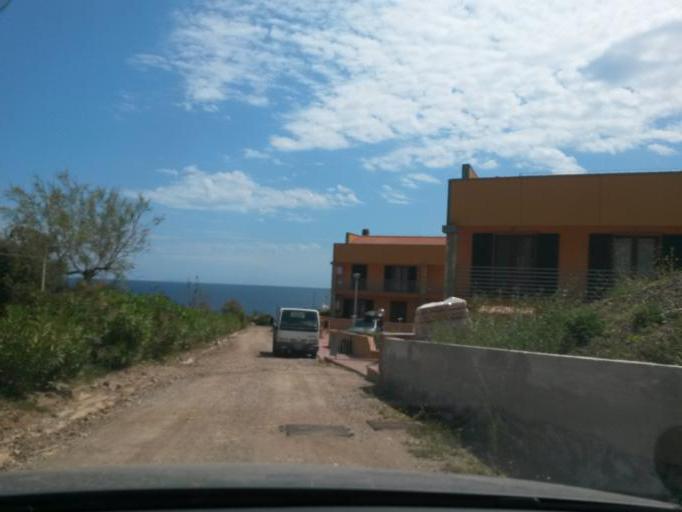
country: IT
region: Tuscany
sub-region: Provincia di Livorno
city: Rio Marina
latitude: 42.8213
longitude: 10.4285
